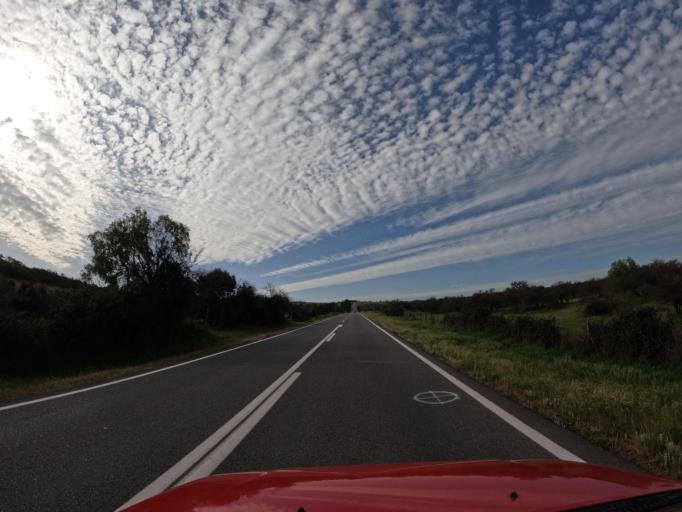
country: CL
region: O'Higgins
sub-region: Provincia de Colchagua
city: Santa Cruz
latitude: -34.2848
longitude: -71.7291
